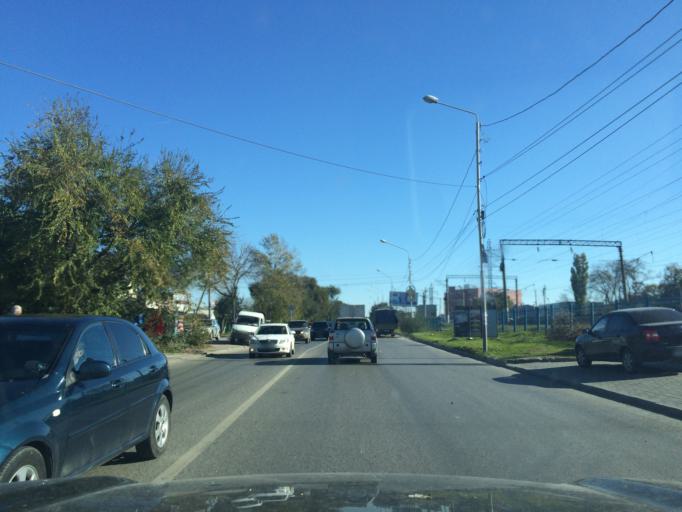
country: RU
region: Rostov
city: Rostov-na-Donu
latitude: 47.2444
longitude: 39.7232
